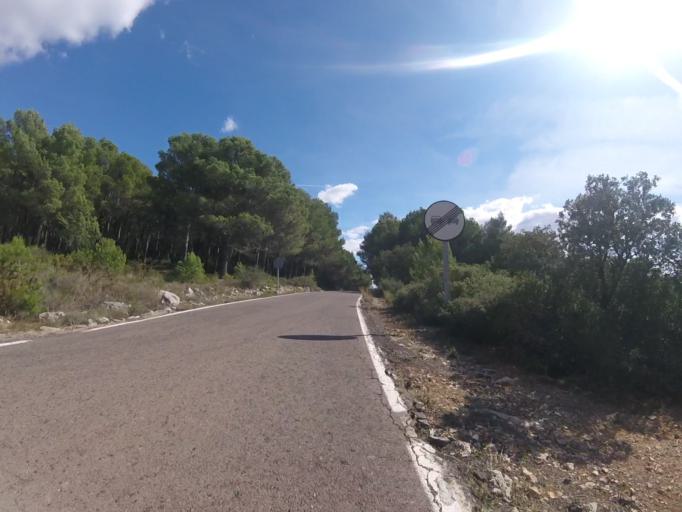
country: ES
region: Valencia
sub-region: Provincia de Castello
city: Albocasser
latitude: 40.4047
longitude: 0.0791
